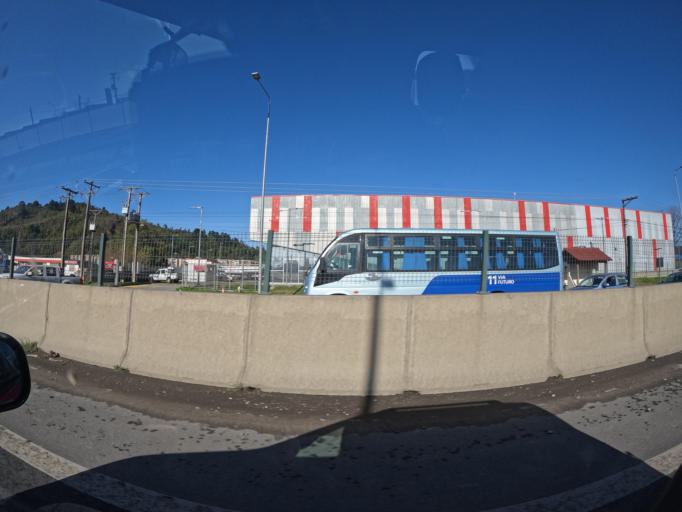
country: CL
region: Biobio
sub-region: Provincia de Concepcion
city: Concepcion
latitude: -36.8182
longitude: -73.0059
